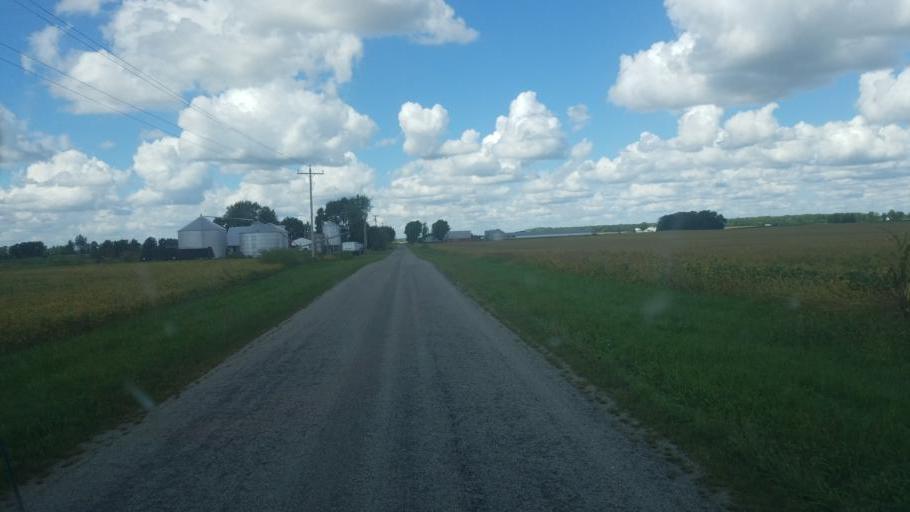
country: US
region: Ohio
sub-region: Union County
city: Richwood
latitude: 40.4486
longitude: -83.4934
